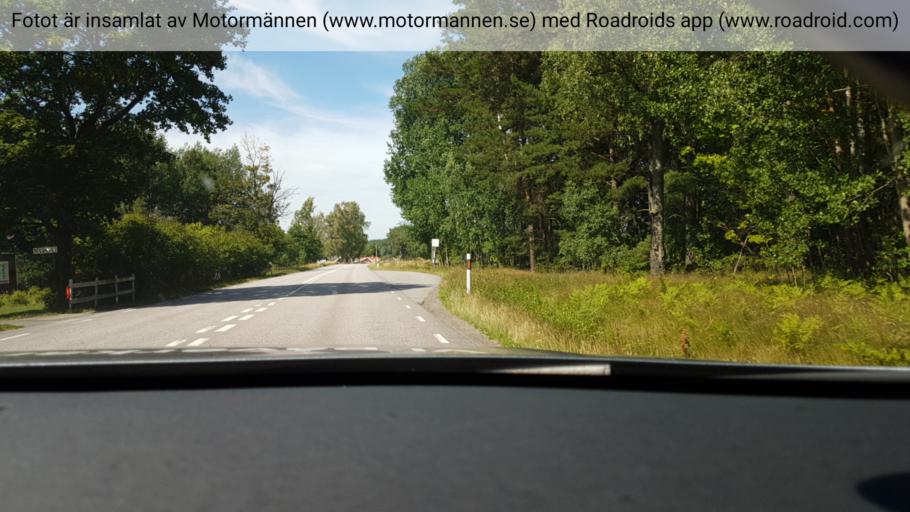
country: SE
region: Vaestra Goetaland
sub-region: Skovde Kommun
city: Stopen
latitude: 58.4690
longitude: 13.9572
